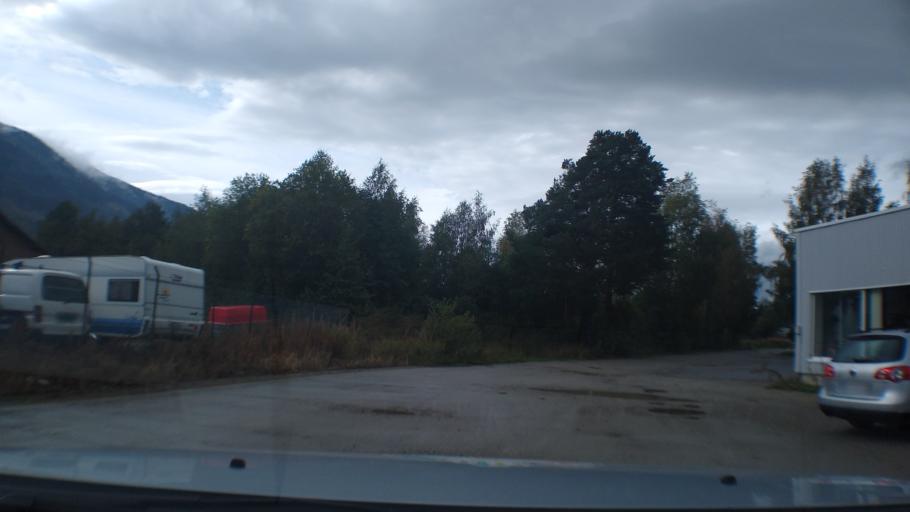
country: NO
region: Oppland
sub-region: Ringebu
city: Ringebu
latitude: 61.5249
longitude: 10.1373
